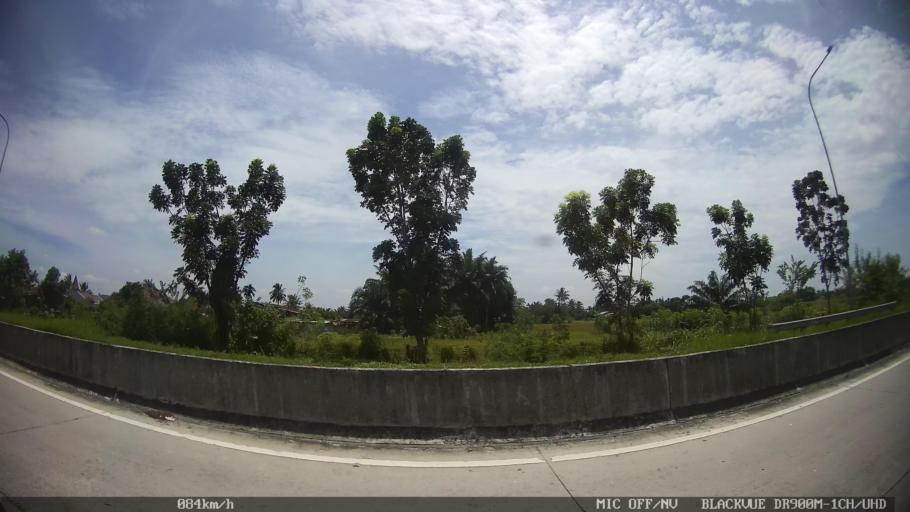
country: ID
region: North Sumatra
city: Perbaungan
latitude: 3.5508
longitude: 98.8882
